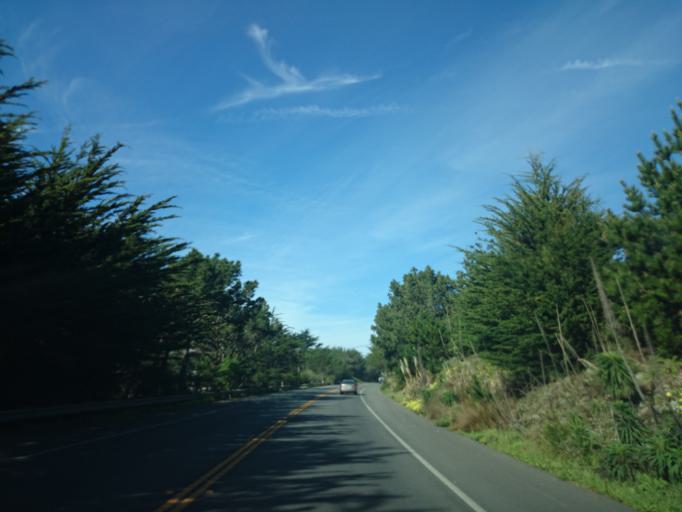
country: US
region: California
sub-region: San Mateo County
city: Moss Beach
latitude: 37.5319
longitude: -122.5171
